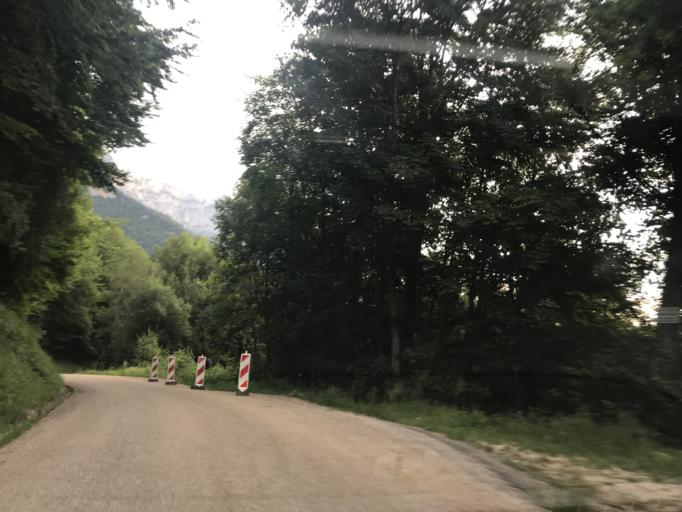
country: FR
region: Rhone-Alpes
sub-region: Departement de l'Isere
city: Le Touvet
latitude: 45.3703
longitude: 5.9228
